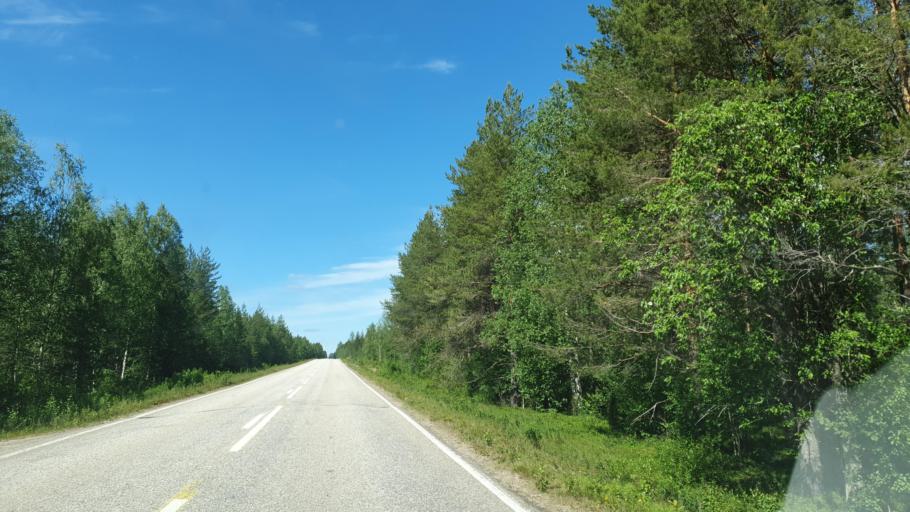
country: FI
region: Kainuu
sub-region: Kehys-Kainuu
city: Suomussalmi
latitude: 64.5681
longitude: 28.8724
